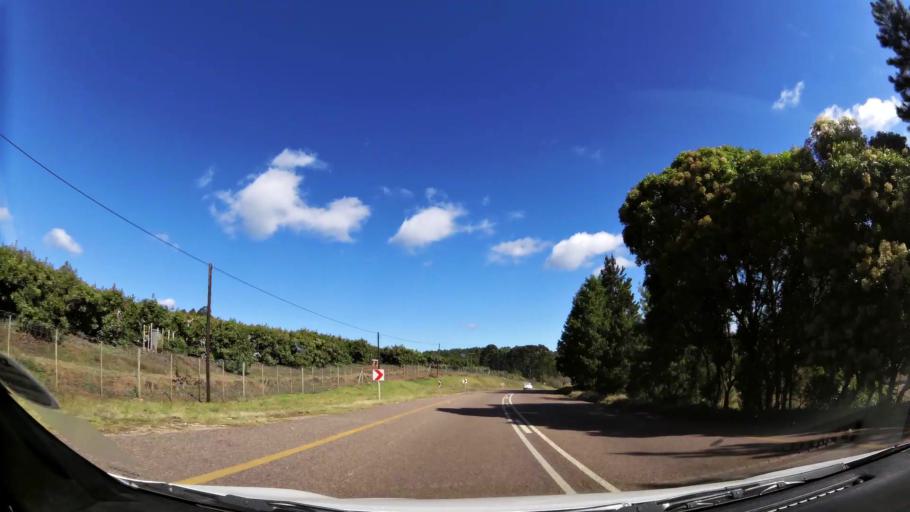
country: ZA
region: Limpopo
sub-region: Capricorn District Municipality
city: Mankoeng
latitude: -23.9004
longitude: 29.9933
